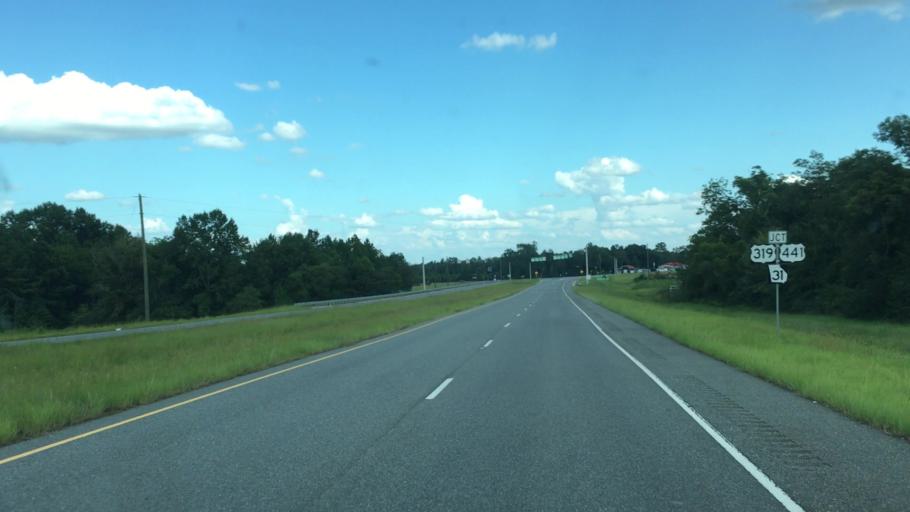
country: US
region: Georgia
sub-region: Laurens County
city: Dublin
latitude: 32.5007
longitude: -82.9332
